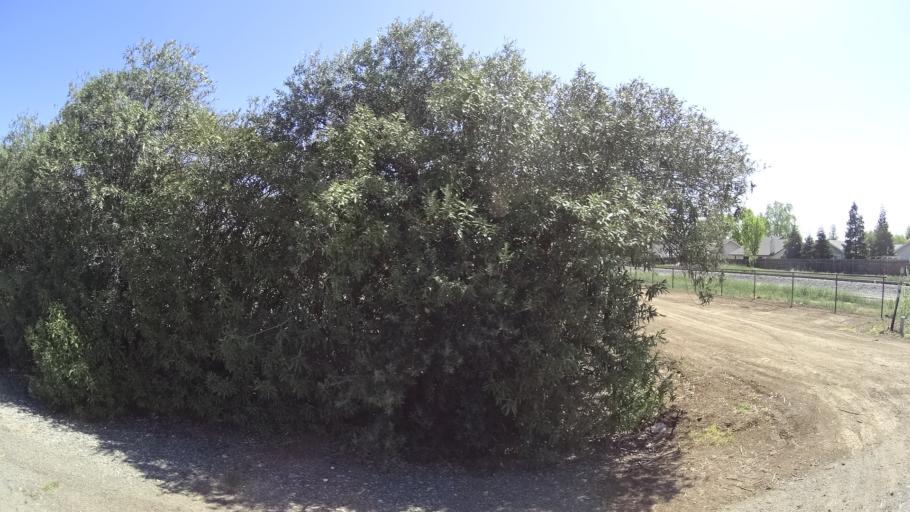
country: US
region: California
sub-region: Glenn County
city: Willows
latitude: 39.5317
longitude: -122.2121
